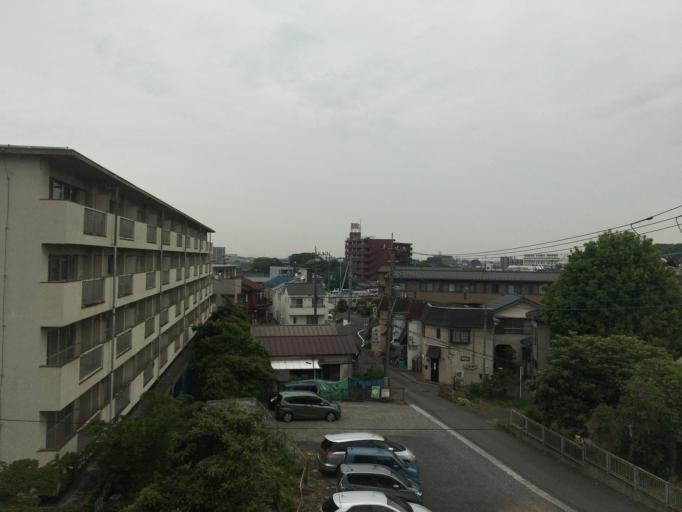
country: JP
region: Saitama
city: Sayama
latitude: 35.8423
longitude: 139.3844
